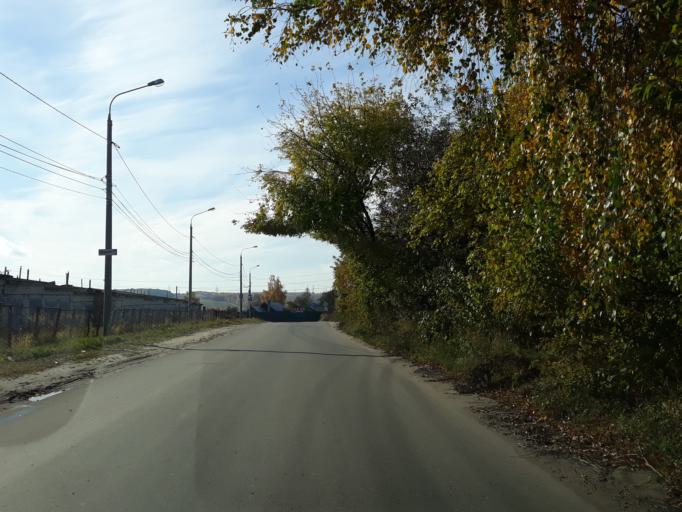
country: RU
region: Nizjnij Novgorod
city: Nizhniy Novgorod
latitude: 56.2370
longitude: 43.9945
